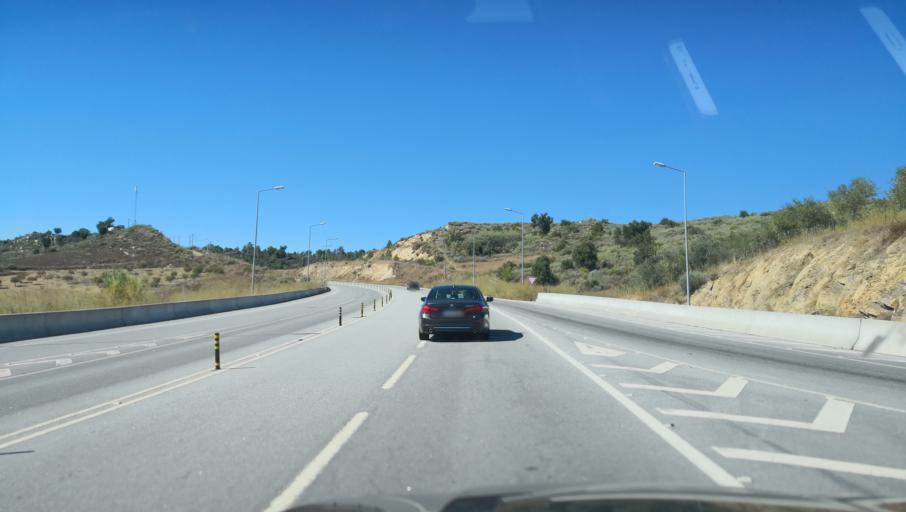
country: PT
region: Vila Real
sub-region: Valpacos
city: Valpacos
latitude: 41.5654
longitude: -7.2709
